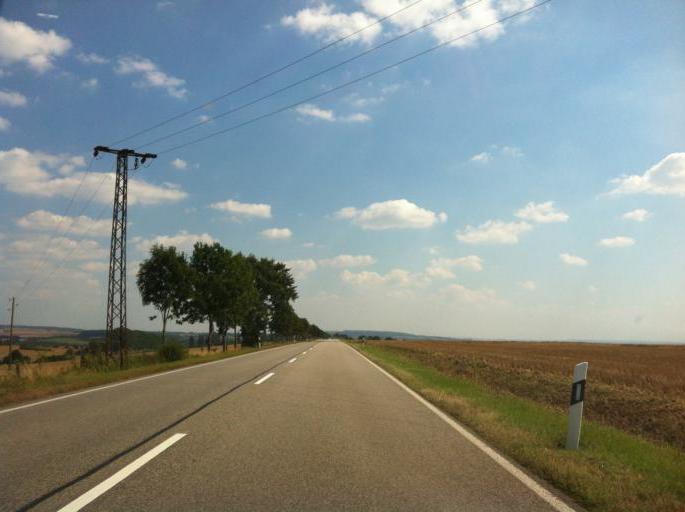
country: DE
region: Thuringia
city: Helmsdorf
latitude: 51.2712
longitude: 10.3831
